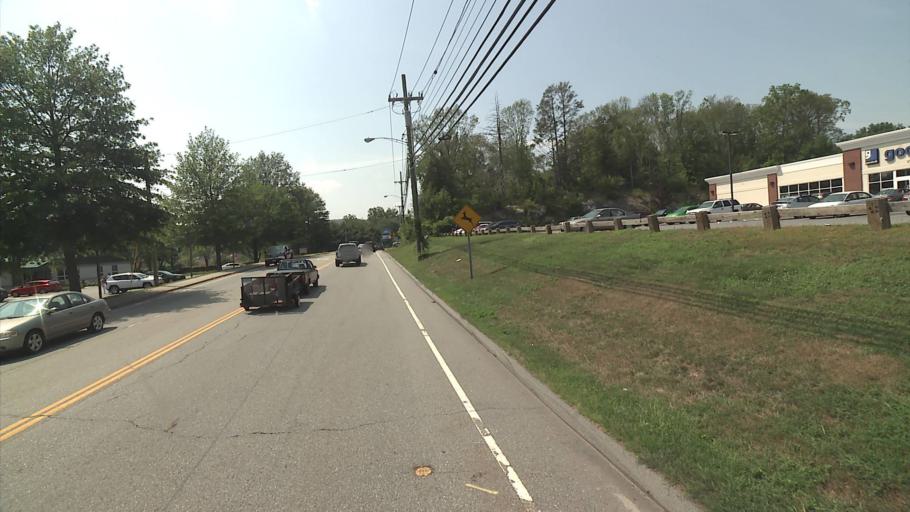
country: US
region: Connecticut
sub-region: New London County
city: Montville Center
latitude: 41.5080
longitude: -72.1205
